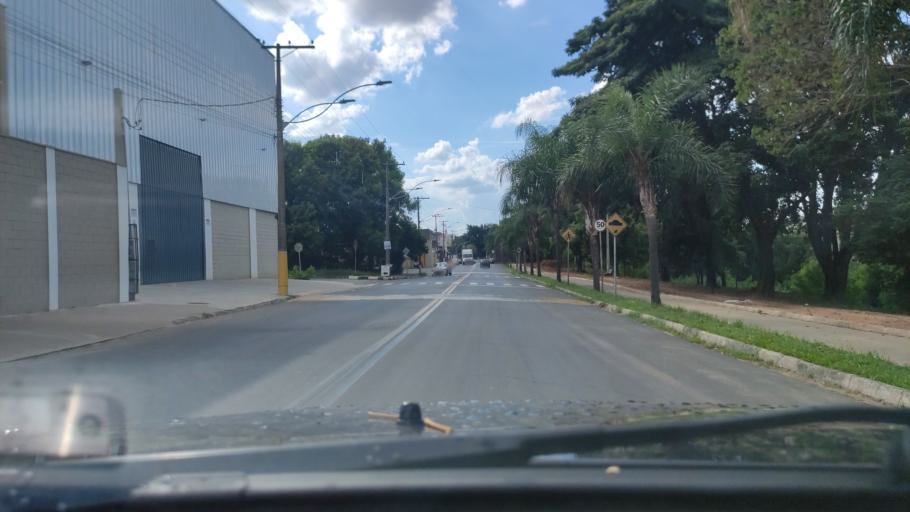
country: BR
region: Sao Paulo
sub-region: Itapira
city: Itapira
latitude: -22.4326
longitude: -46.8210
